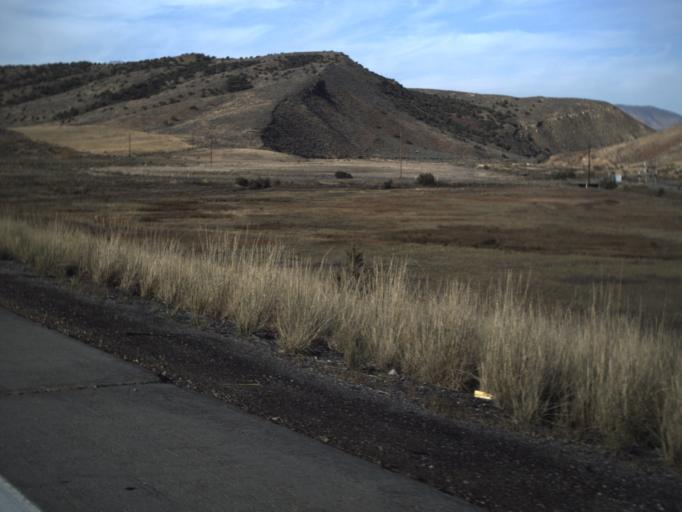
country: US
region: Utah
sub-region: Juab County
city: Nephi
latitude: 39.4861
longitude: -111.9762
